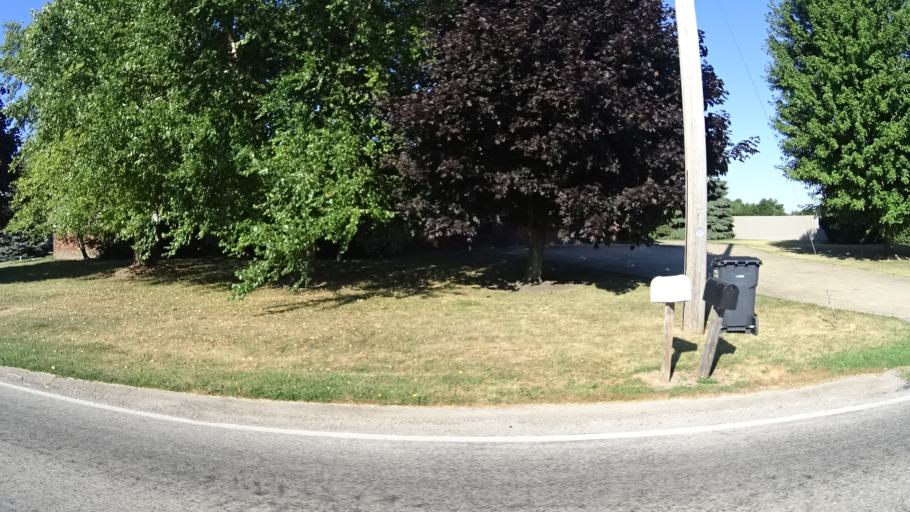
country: US
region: Ohio
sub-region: Erie County
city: Sandusky
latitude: 41.3733
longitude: -82.7669
